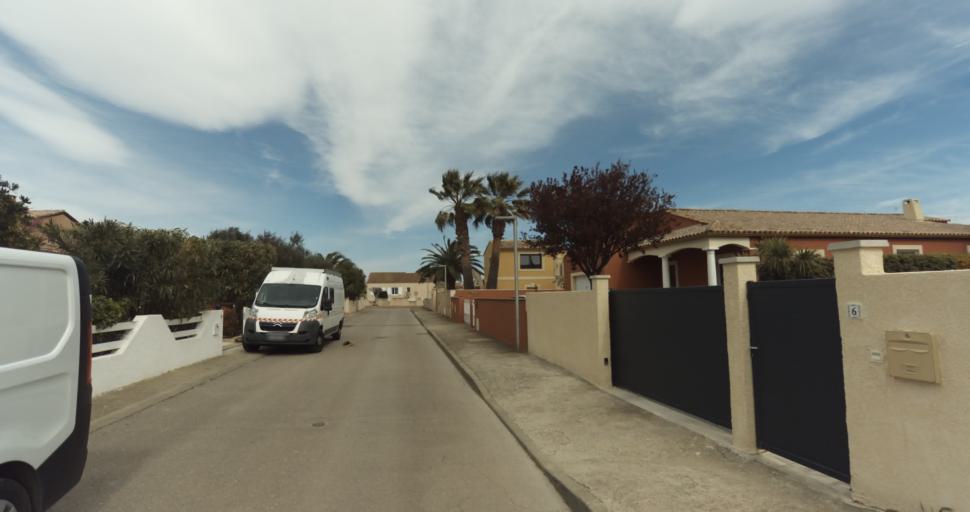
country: FR
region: Languedoc-Roussillon
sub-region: Departement de l'Herault
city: Marseillan
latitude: 43.3376
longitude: 3.5300
